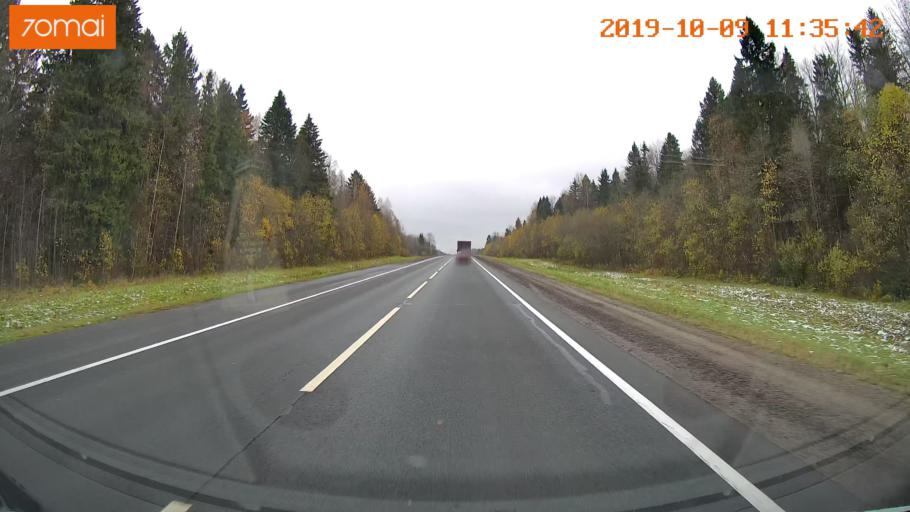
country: RU
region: Vologda
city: Gryazovets
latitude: 59.0000
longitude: 40.1288
